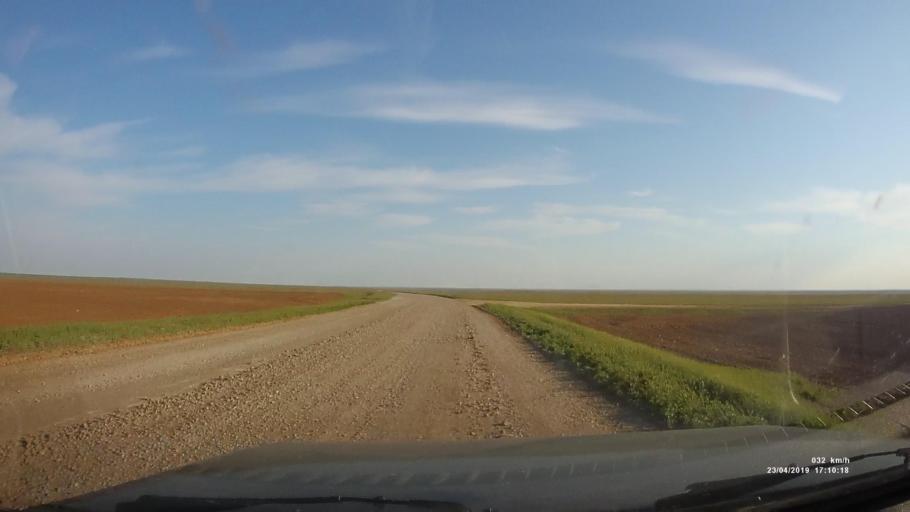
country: RU
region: Kalmykiya
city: Priyutnoye
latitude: 46.2474
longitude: 43.4841
